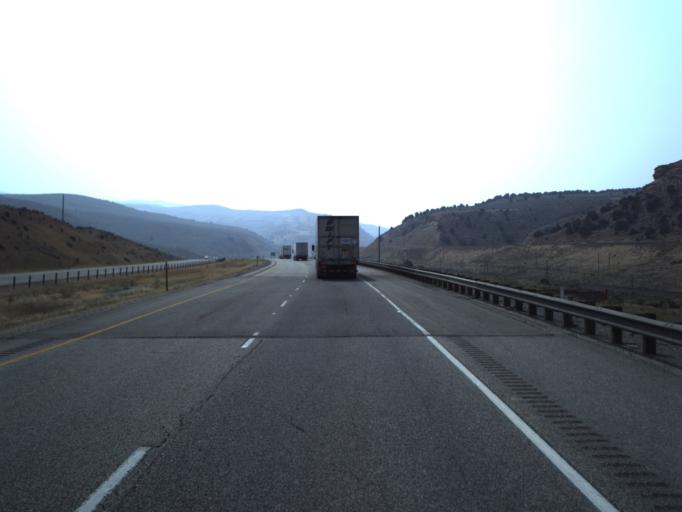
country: US
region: Utah
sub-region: Summit County
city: Coalville
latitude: 41.0986
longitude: -111.2167
